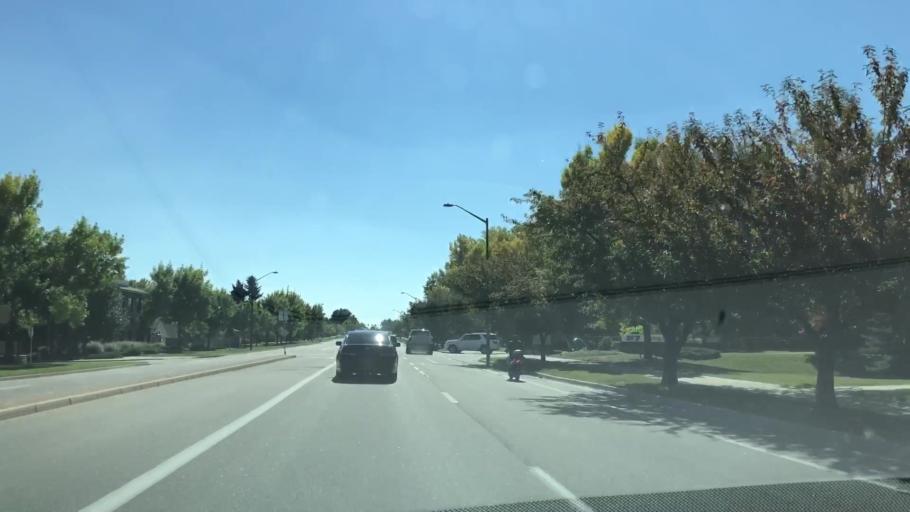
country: US
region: Colorado
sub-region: Larimer County
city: Fort Collins
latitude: 40.5360
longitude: -105.0393
